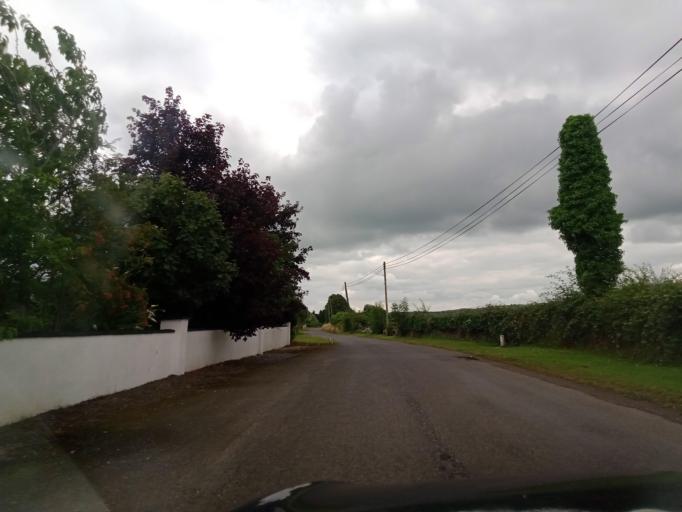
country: IE
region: Leinster
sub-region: Laois
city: Stradbally
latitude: 52.9731
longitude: -7.1544
